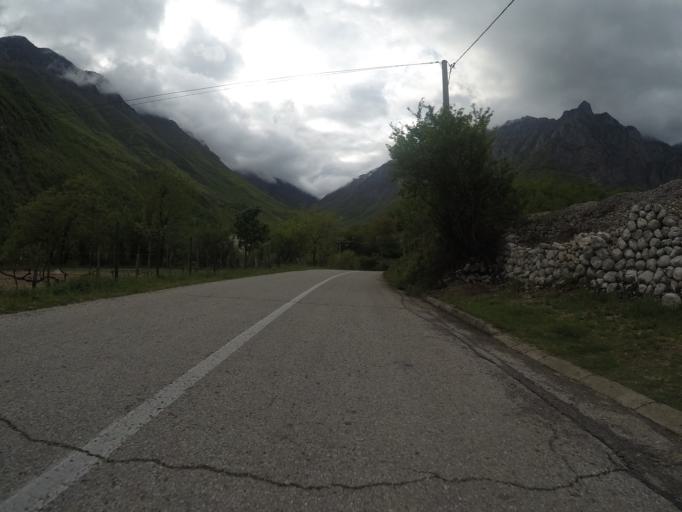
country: BA
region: Federation of Bosnia and Herzegovina
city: Siroki Brijeg
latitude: 43.5421
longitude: 17.5591
